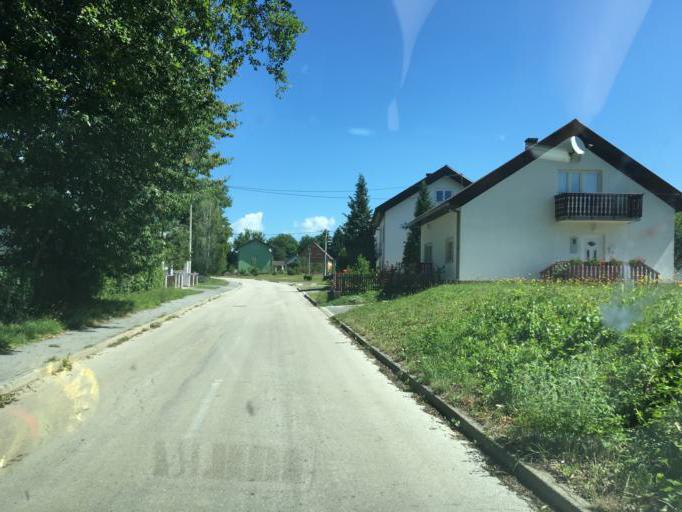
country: HR
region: Licko-Senjska
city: Gospic
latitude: 44.5451
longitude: 15.3574
